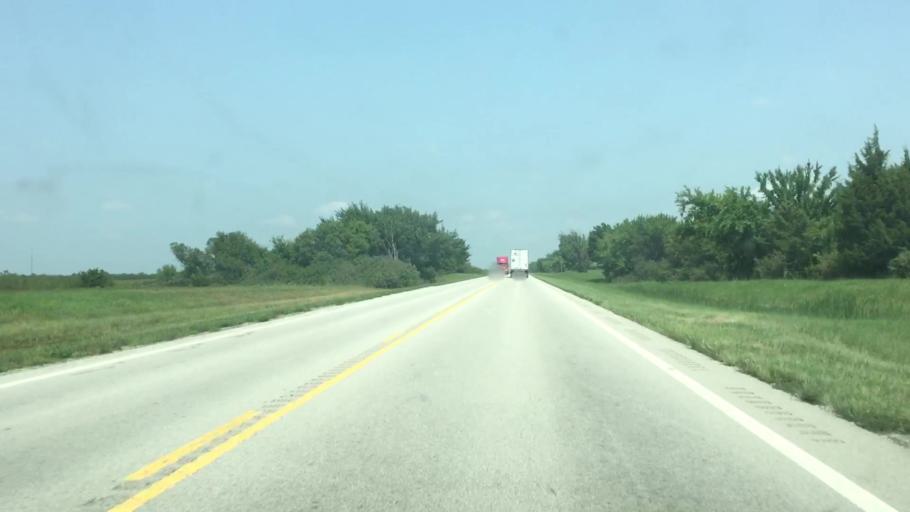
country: US
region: Kansas
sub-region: Allen County
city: Iola
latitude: 38.1087
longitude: -95.3510
